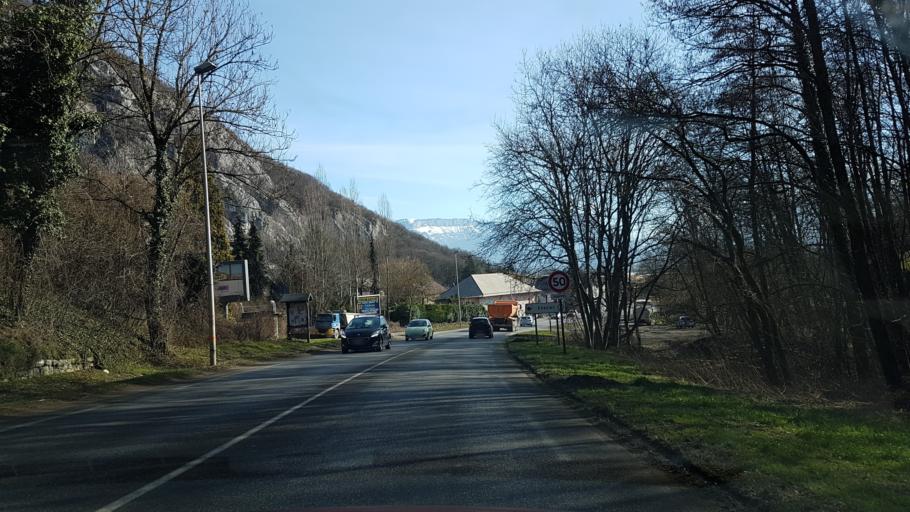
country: FR
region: Rhone-Alpes
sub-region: Departement de la Haute-Savoie
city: Poisy
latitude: 45.9434
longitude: 6.0577
